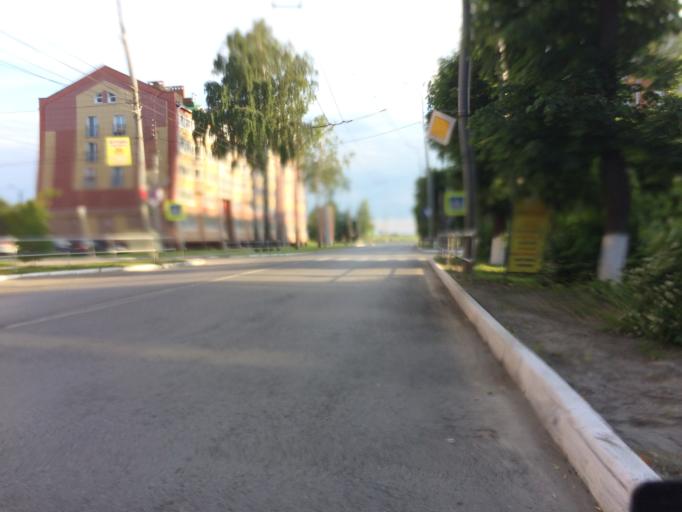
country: RU
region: Mariy-El
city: Medvedevo
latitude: 56.6374
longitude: 47.8029
